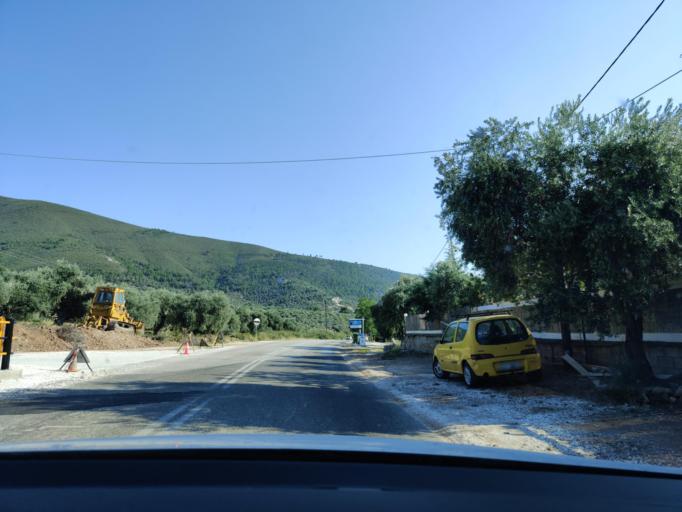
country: GR
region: East Macedonia and Thrace
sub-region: Nomos Kavalas
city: Prinos
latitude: 40.6884
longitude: 24.5267
